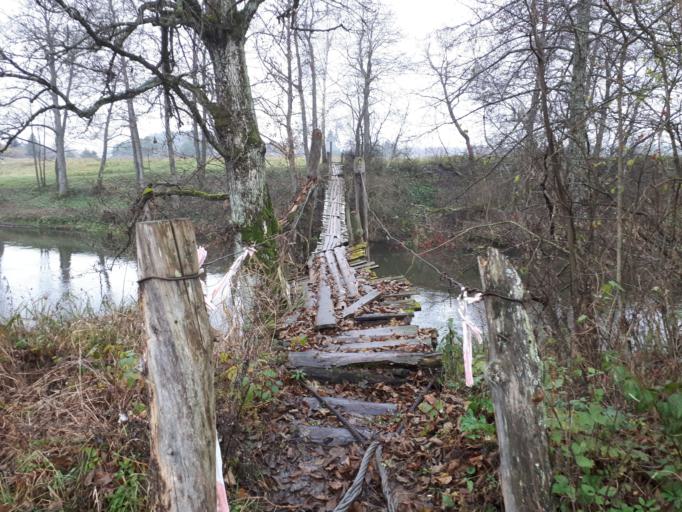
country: LT
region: Alytaus apskritis
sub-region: Alytaus rajonas
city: Daugai
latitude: 54.1883
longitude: 24.3206
